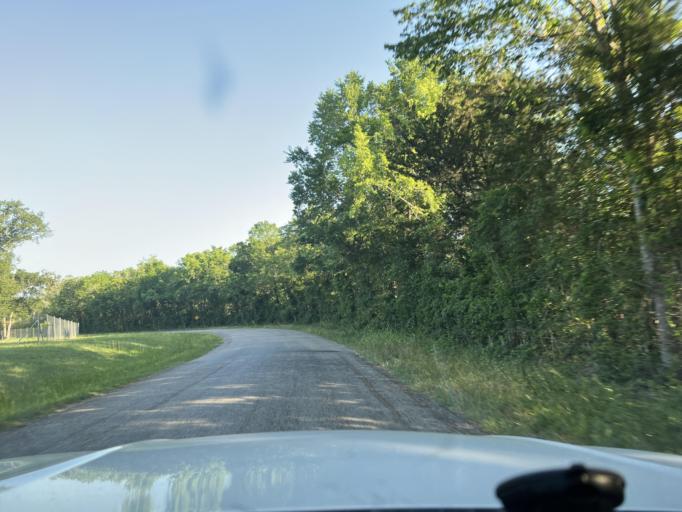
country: US
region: Texas
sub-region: Washington County
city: Brenham
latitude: 30.2100
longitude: -96.3753
